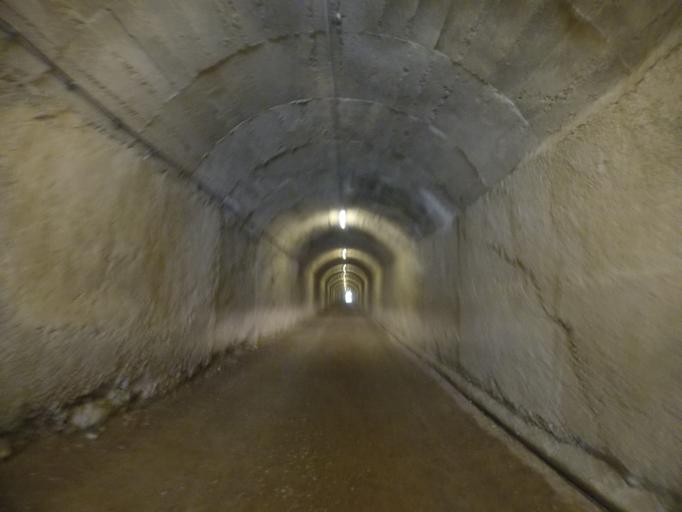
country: AL
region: Tirane
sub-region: Rrethi i Tiranes
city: Farka e Madhe
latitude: 41.3499
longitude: 19.8607
